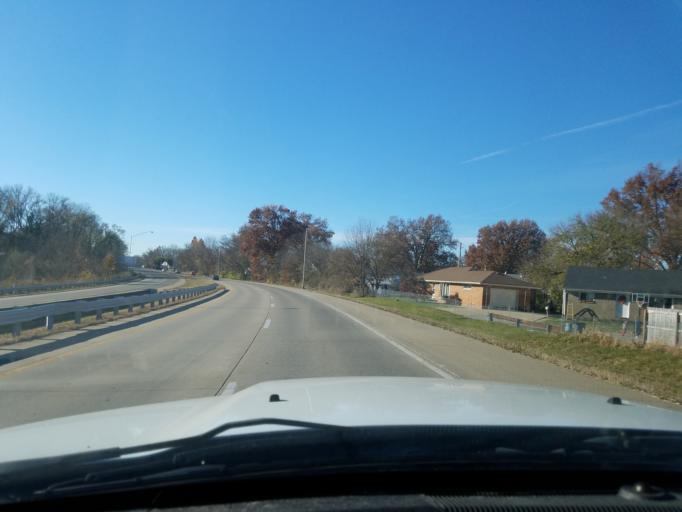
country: US
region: Indiana
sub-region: Clark County
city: Clarksville
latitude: 38.2922
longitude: -85.7611
